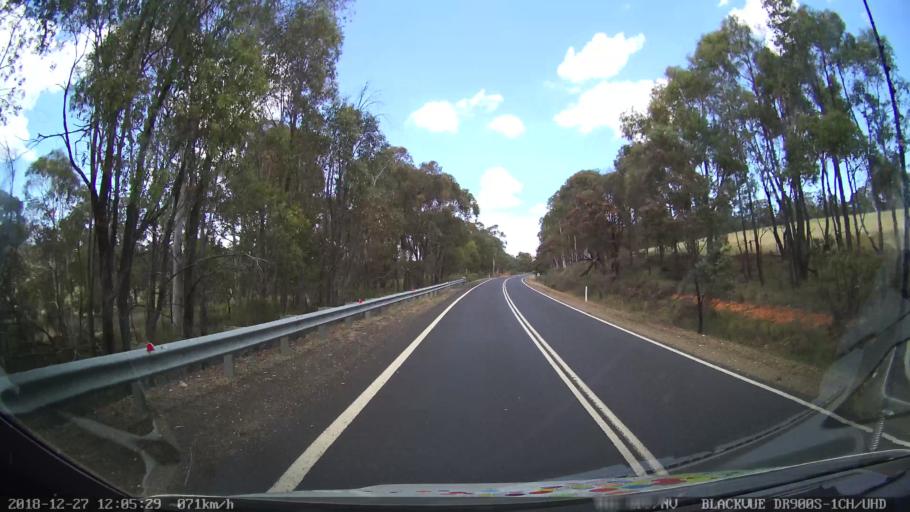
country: AU
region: New South Wales
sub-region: Blayney
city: Blayney
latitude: -33.8026
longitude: 149.3382
